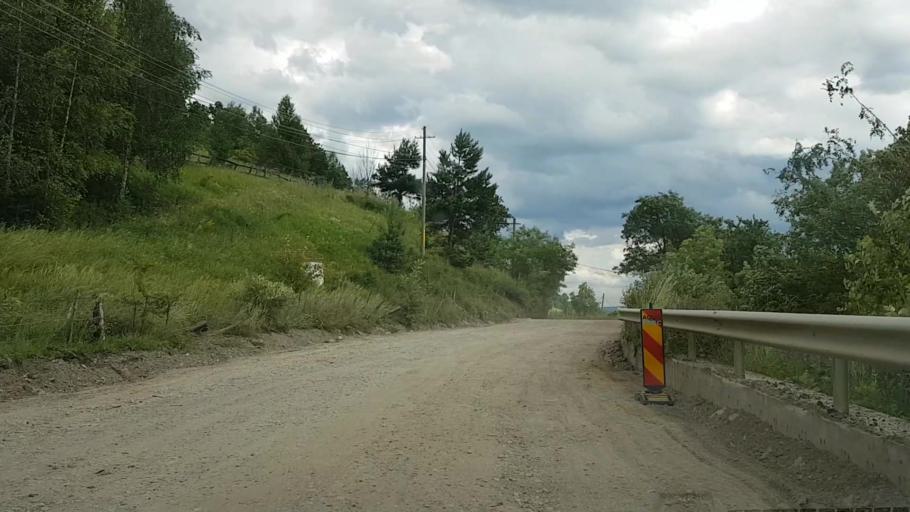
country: RO
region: Neamt
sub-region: Comuna Hangu
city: Hangu
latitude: 47.0382
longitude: 26.0589
